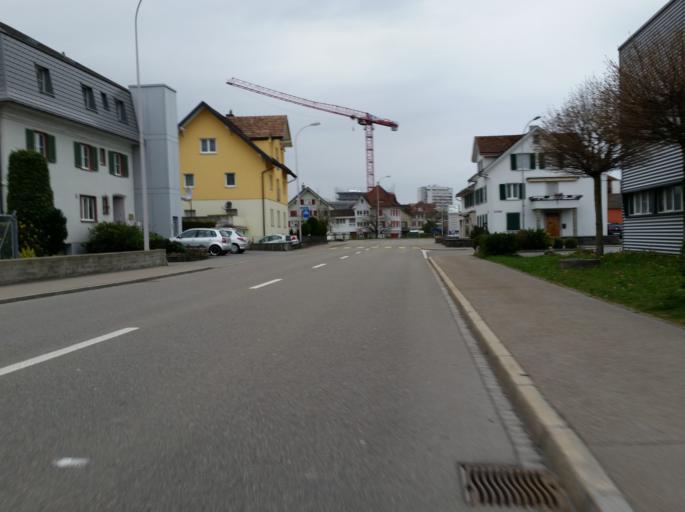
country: CH
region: Saint Gallen
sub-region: Wahlkreis Rheintal
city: Sankt Margrethen
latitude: 47.4493
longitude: 9.6380
